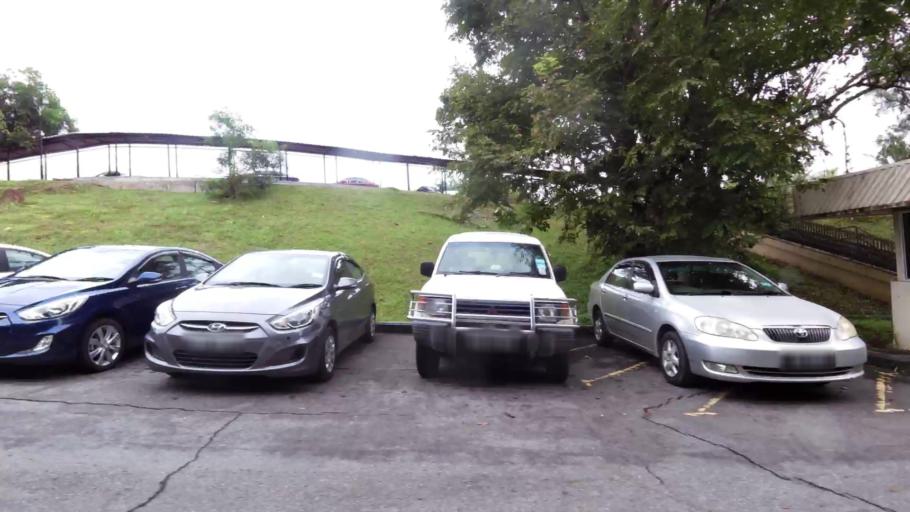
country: BN
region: Brunei and Muara
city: Bandar Seri Begawan
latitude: 4.8941
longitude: 114.9340
